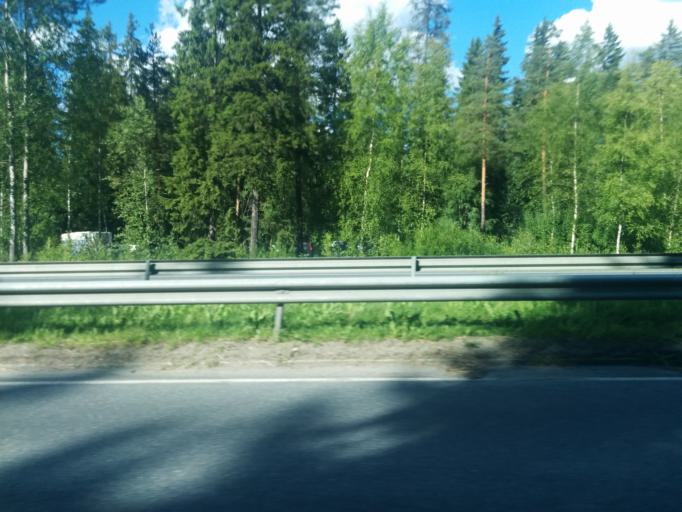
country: FI
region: Pirkanmaa
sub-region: Tampere
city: Tampere
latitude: 61.5022
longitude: 23.8663
